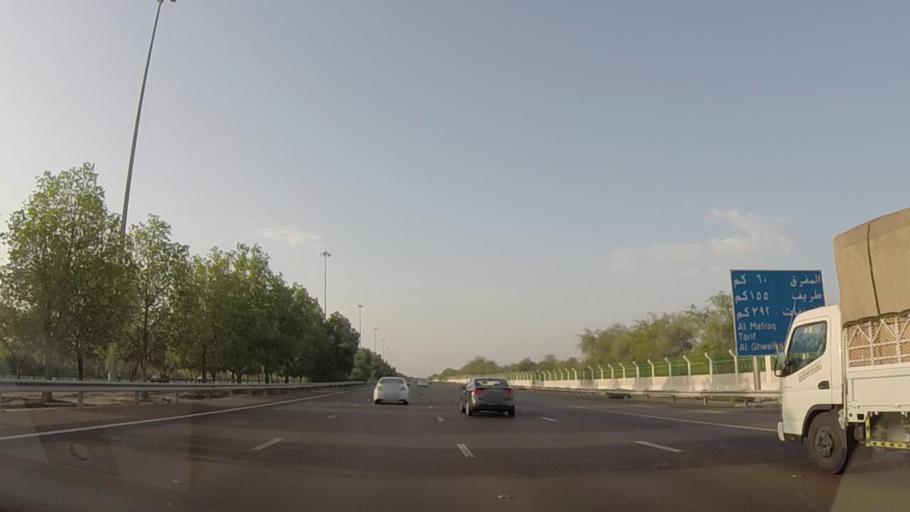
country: AE
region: Dubai
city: Dubai
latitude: 24.7779
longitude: 54.8528
